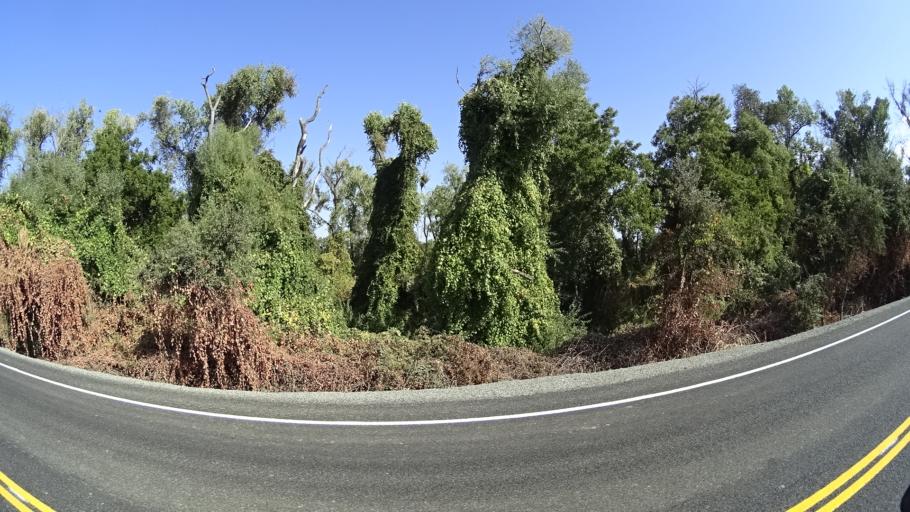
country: US
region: California
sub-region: Yolo County
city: West Sacramento
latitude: 38.6568
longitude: -121.6080
